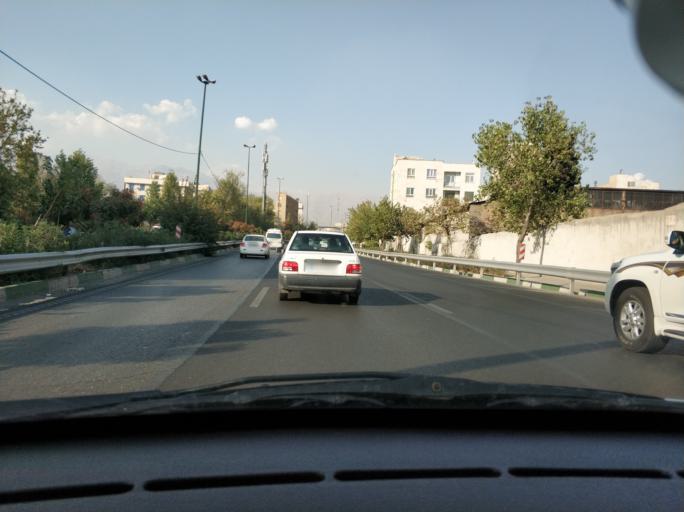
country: IR
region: Tehran
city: Tehran
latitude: 35.7463
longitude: 51.4640
